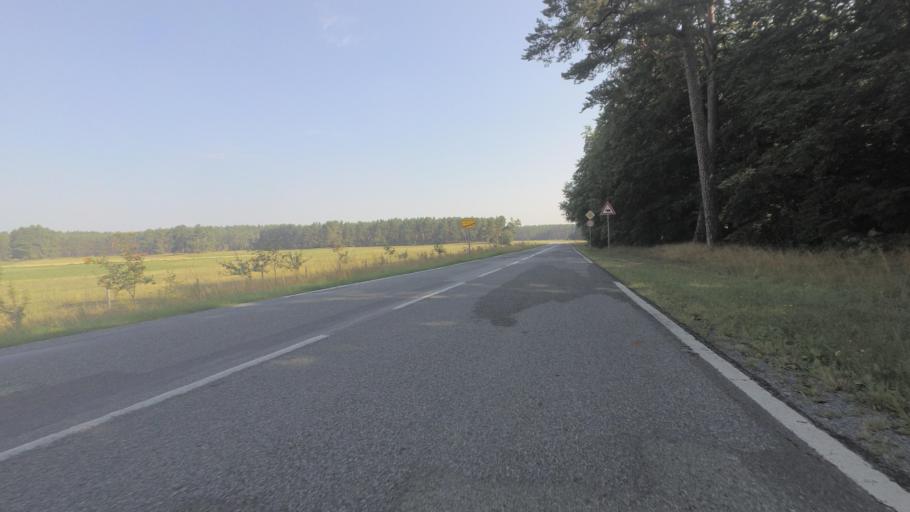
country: DE
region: Mecklenburg-Vorpommern
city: Malchow
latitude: 53.5387
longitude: 12.4293
